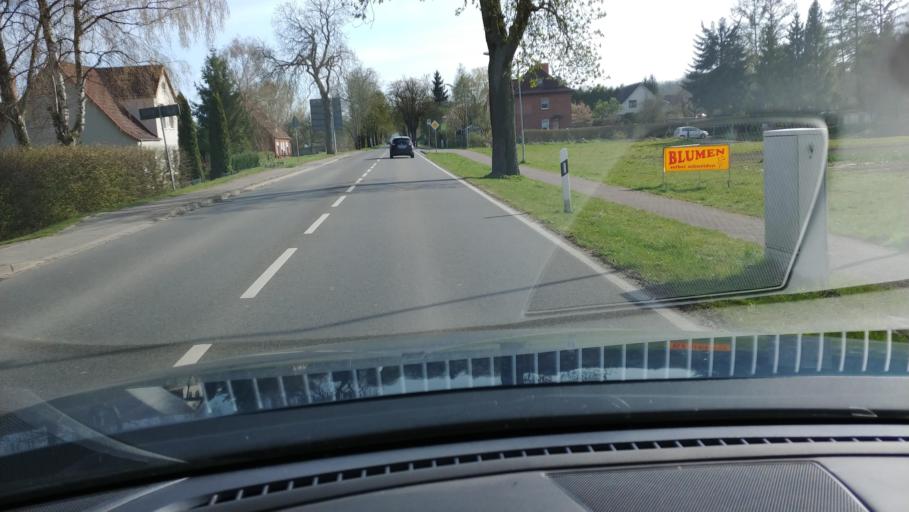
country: DE
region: Mecklenburg-Vorpommern
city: Lubstorf
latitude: 53.7288
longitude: 11.4036
